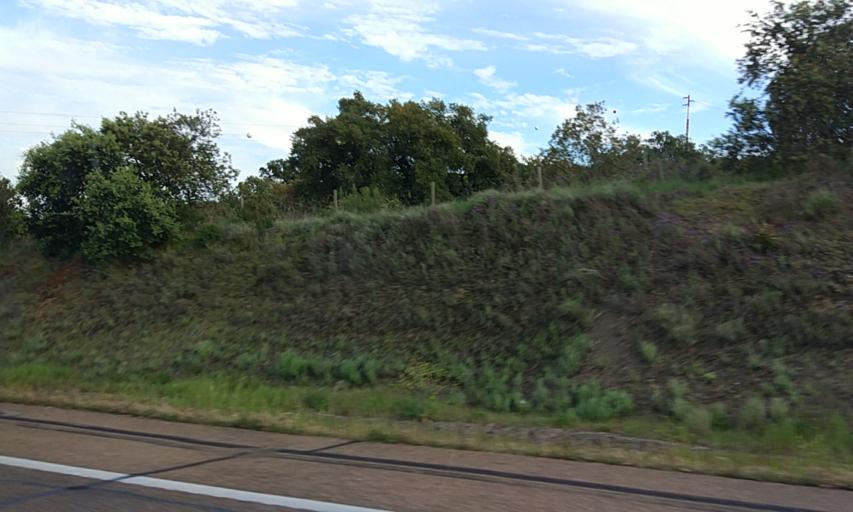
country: PT
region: Portalegre
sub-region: Elvas
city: Elvas
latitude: 38.9093
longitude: -7.1734
